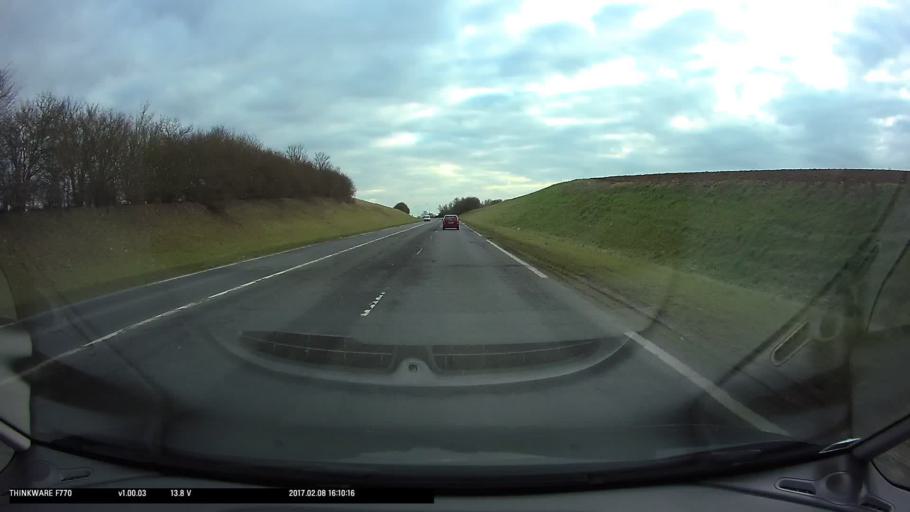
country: FR
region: Ile-de-France
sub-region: Departement du Val-d'Oise
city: Ableiges
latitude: 49.1158
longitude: 2.0299
